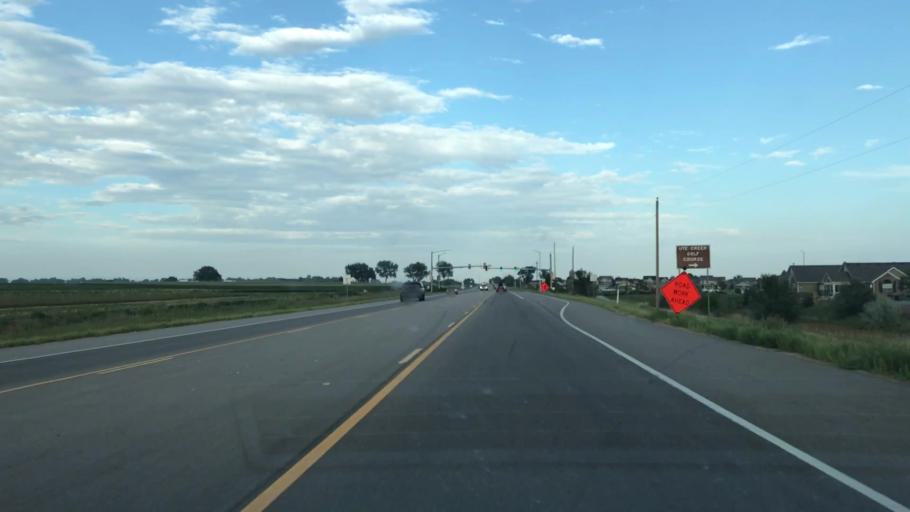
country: US
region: Colorado
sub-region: Boulder County
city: Longmont
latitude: 40.2032
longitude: -105.0769
